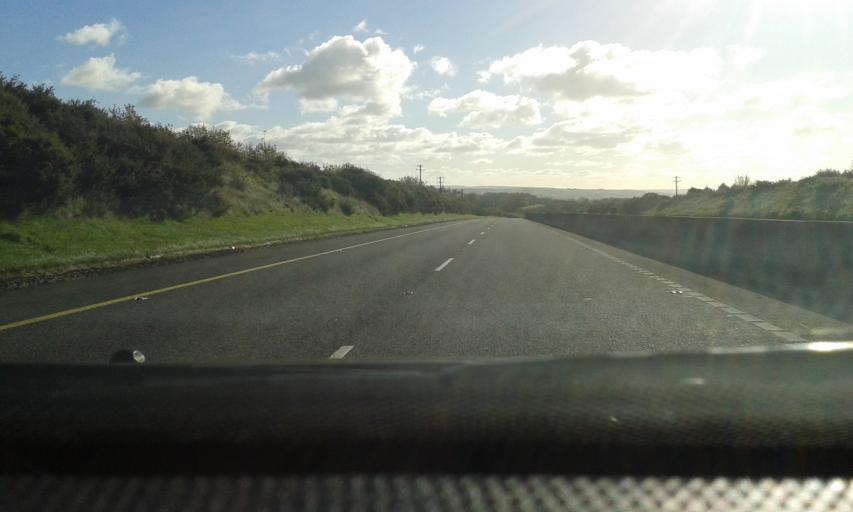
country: IE
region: Munster
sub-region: County Cork
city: Mitchelstown
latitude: 52.2118
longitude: -8.2767
